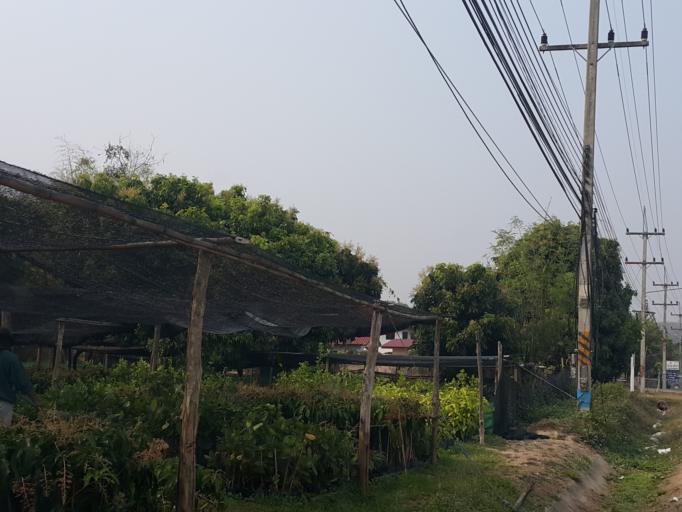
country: TH
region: Chiang Mai
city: San Sai
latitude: 18.9602
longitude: 98.9441
